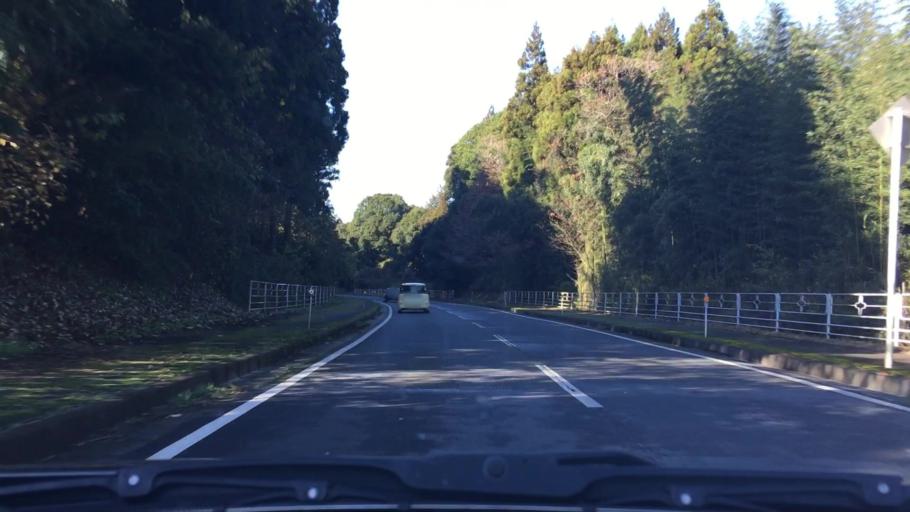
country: JP
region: Chiba
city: Sawara
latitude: 35.8092
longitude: 140.4806
